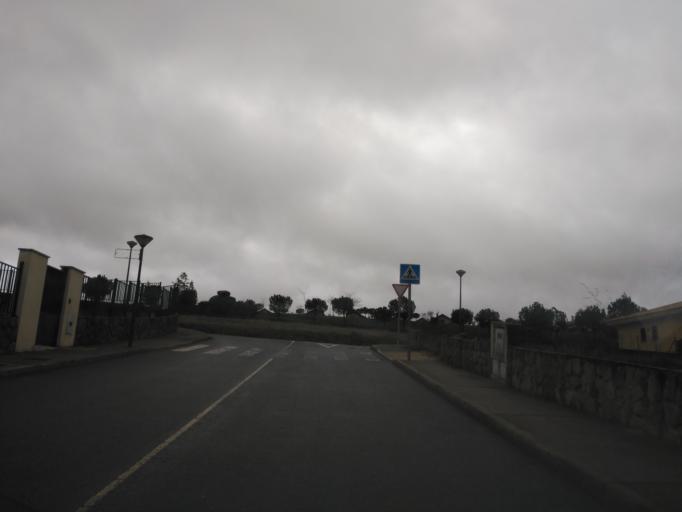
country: ES
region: Castille and Leon
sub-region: Provincia de Salamanca
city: Villamayor
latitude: 40.9811
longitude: -5.7000
